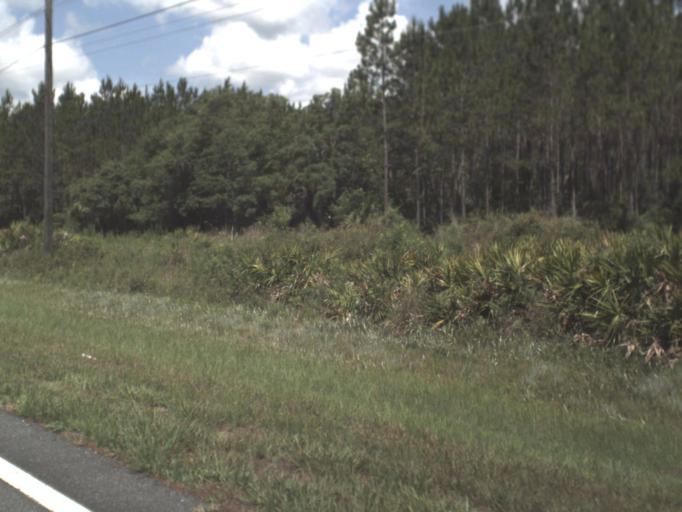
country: US
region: Florida
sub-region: Levy County
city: Chiefland
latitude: 29.2491
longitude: -82.9091
